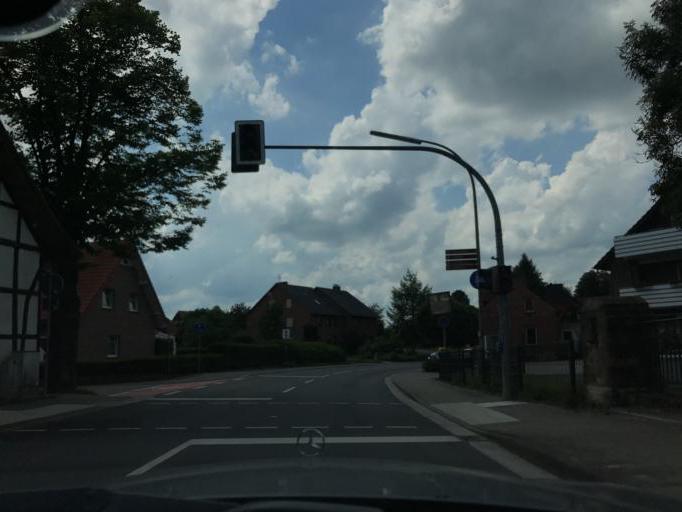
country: DE
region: Lower Saxony
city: Hagen
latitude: 52.1969
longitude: 7.9681
